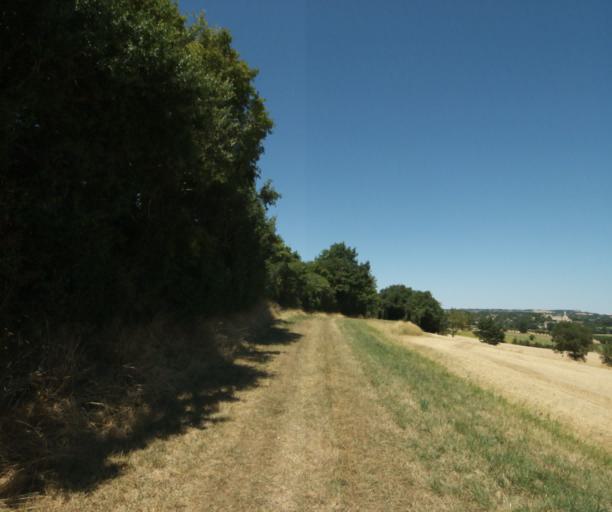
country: FR
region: Midi-Pyrenees
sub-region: Departement de la Haute-Garonne
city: Saint-Felix-Lauragais
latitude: 43.4665
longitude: 1.9223
